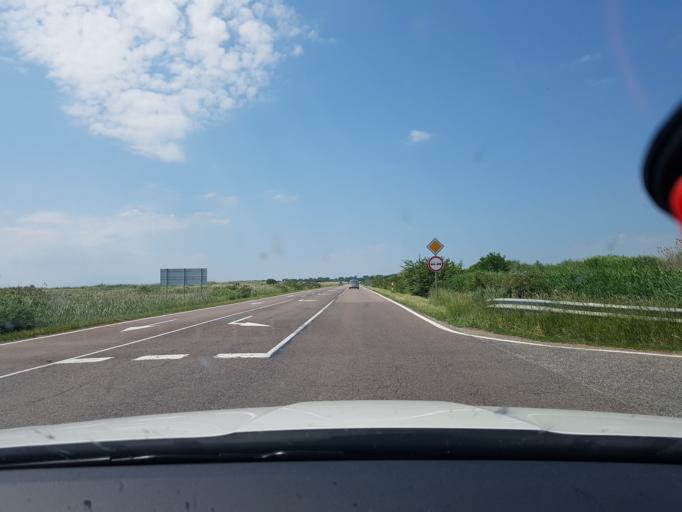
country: HU
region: Hajdu-Bihar
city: Tiszacsege
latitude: 47.5884
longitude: 21.0285
